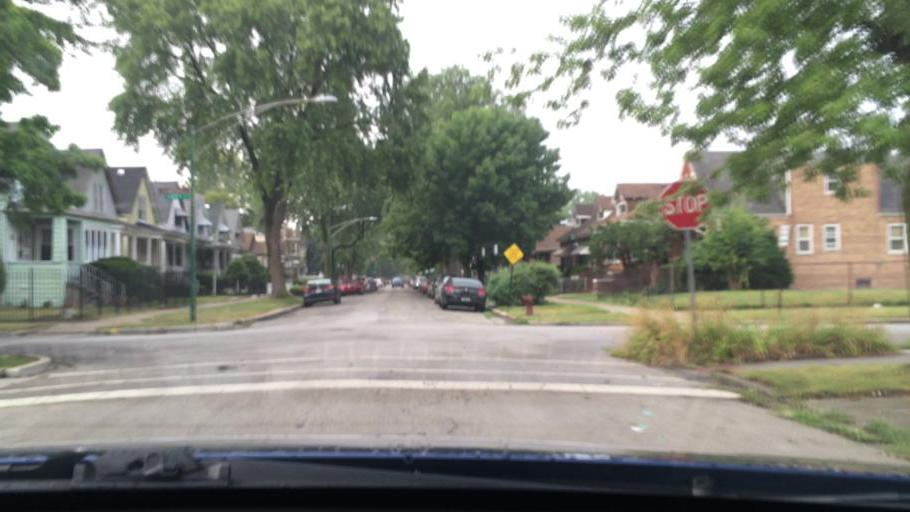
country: US
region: Illinois
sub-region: Cook County
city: Evergreen Park
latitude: 41.7416
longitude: -87.6499
